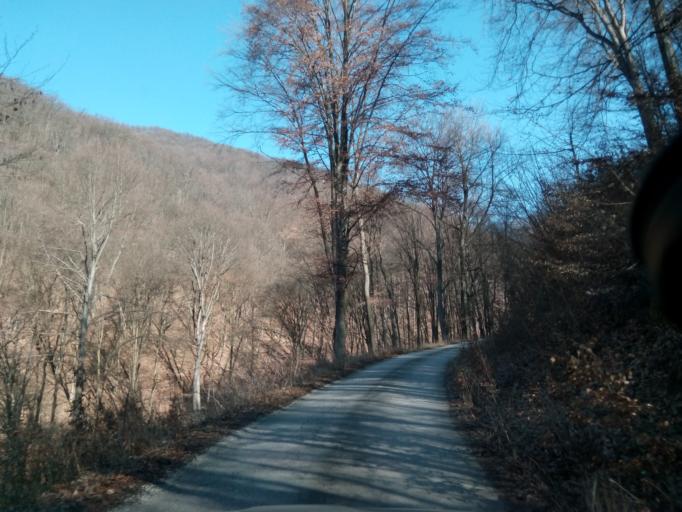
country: SK
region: Kosicky
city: Roznava
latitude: 48.5523
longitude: 20.5693
